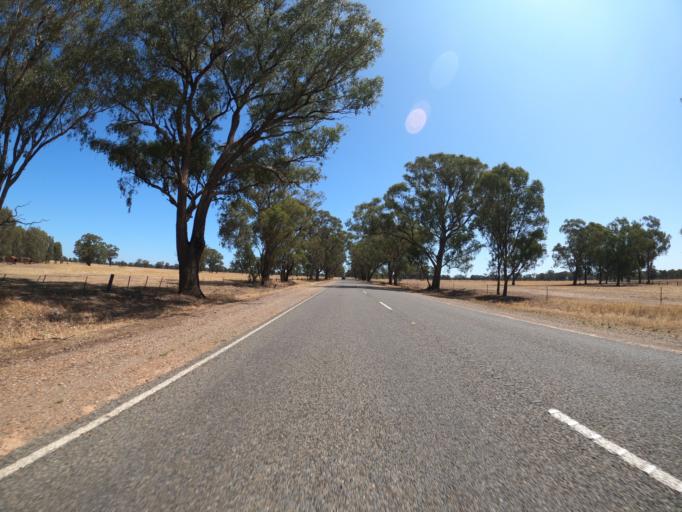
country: AU
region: New South Wales
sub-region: Corowa Shire
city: Corowa
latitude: -36.0701
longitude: 146.3566
